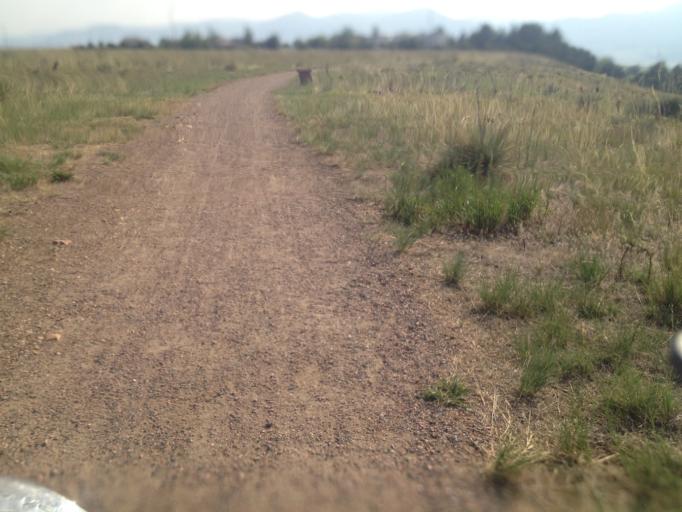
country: US
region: Colorado
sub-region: Boulder County
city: Superior
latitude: 39.9768
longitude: -105.1722
